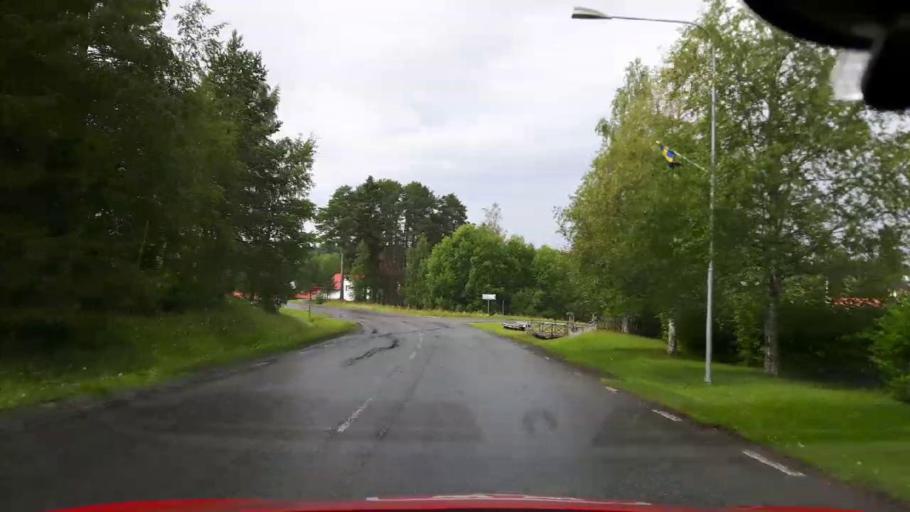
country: SE
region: Jaemtland
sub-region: Krokoms Kommun
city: Krokom
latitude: 63.3476
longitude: 14.2587
